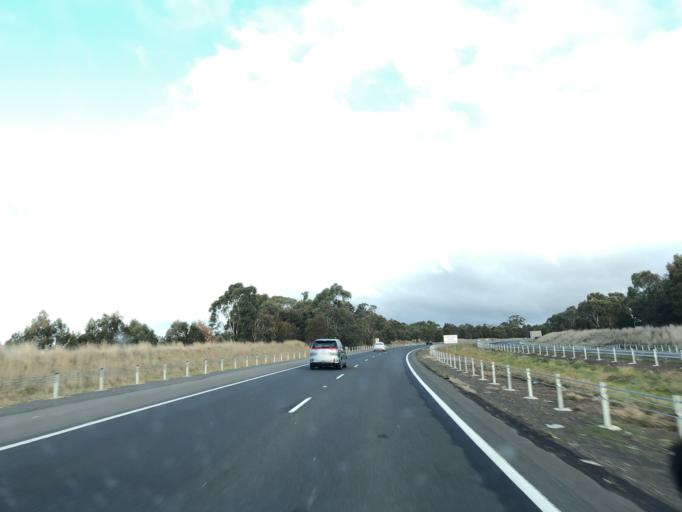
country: AU
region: Victoria
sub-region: Mount Alexander
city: Castlemaine
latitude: -37.2468
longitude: 144.4715
